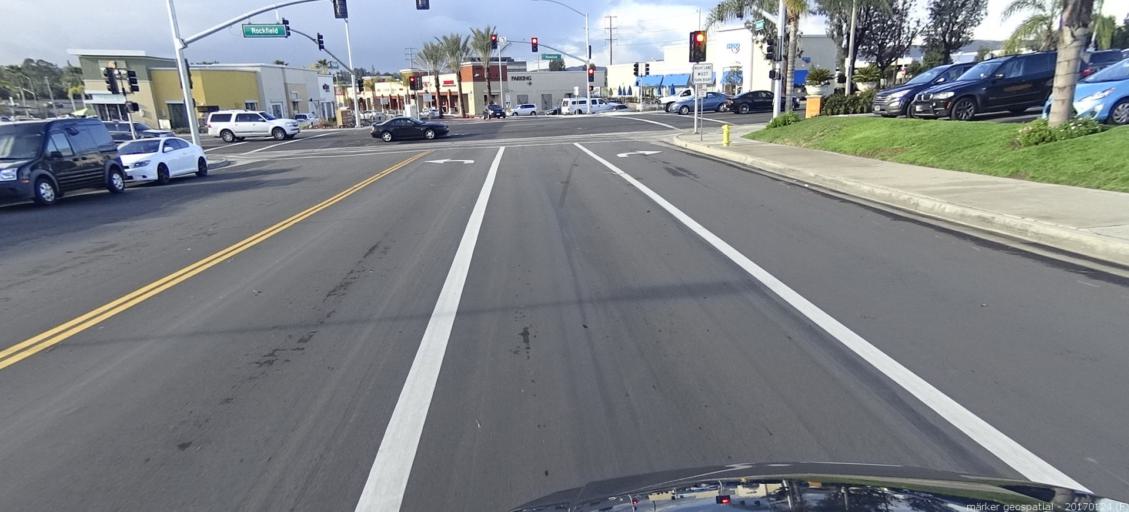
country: US
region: California
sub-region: Orange County
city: Laguna Hills
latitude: 33.6310
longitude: -117.7178
